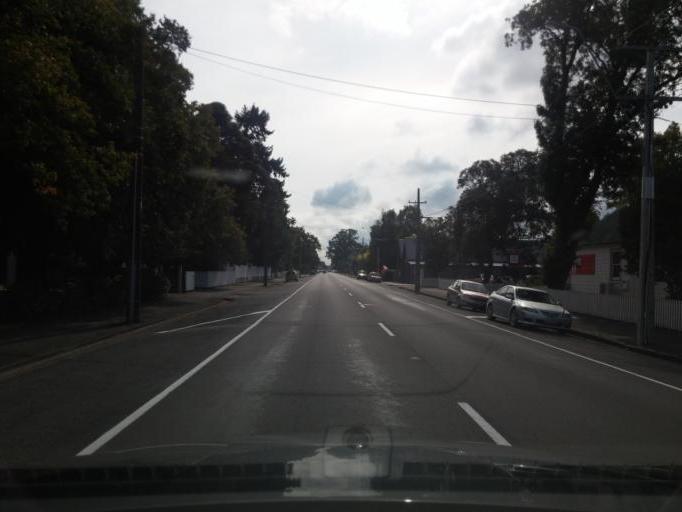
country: NZ
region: Wellington
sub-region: Masterton District
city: Masterton
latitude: -41.0857
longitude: 175.4545
